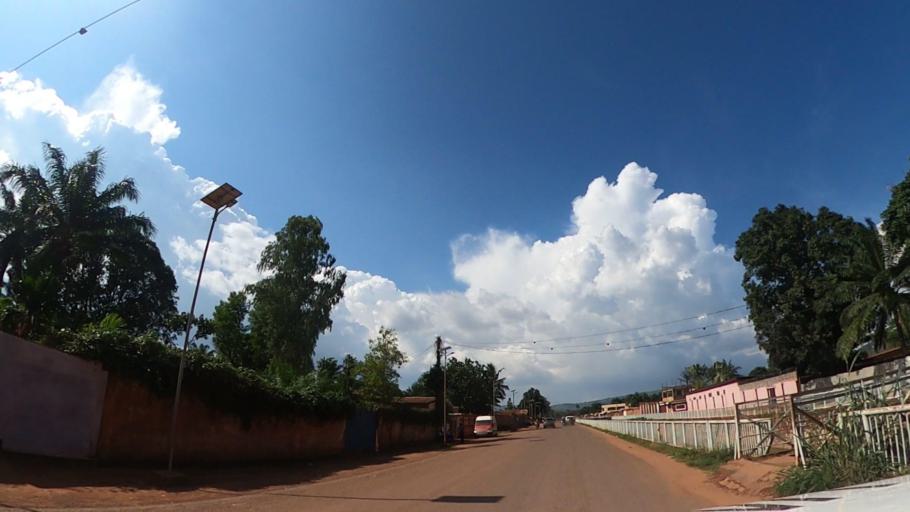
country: CF
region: Bangui
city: Bangui
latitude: 4.3744
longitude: 18.5529
